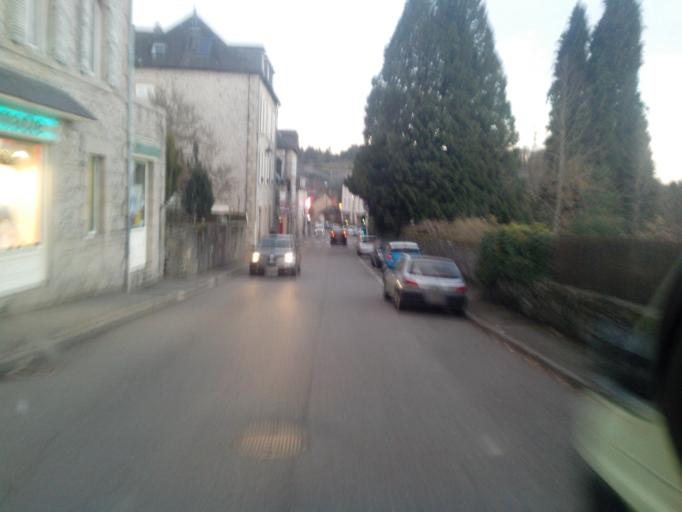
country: FR
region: Limousin
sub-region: Departement de la Correze
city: Meymac
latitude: 45.5355
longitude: 2.1459
